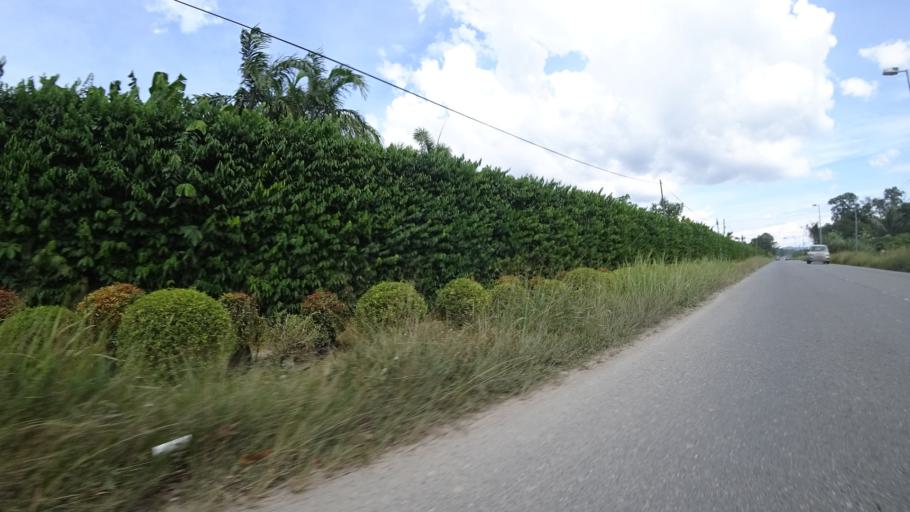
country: BN
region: Brunei and Muara
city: Bandar Seri Begawan
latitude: 4.8445
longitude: 114.8550
